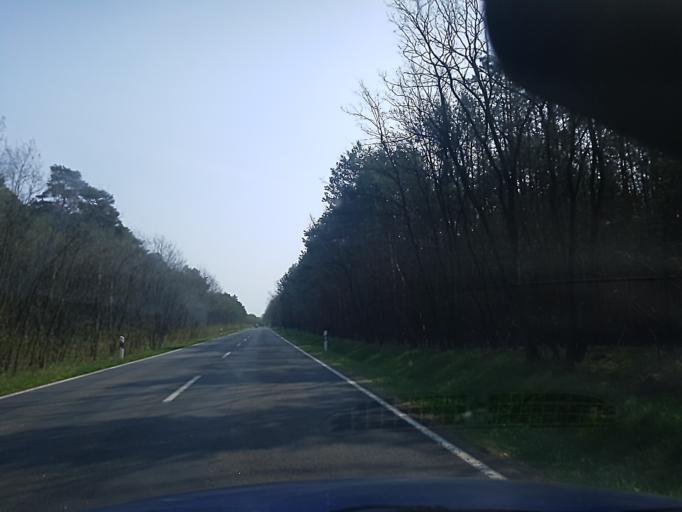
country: DE
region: Saxony
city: Beilrode
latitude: 51.5906
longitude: 13.1050
